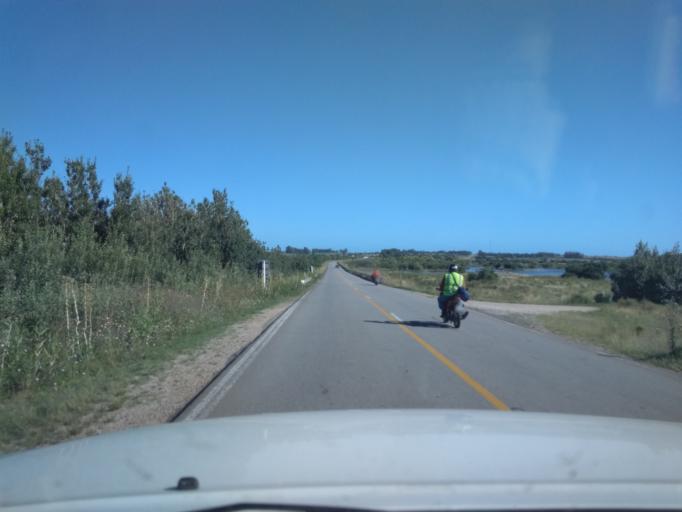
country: UY
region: Canelones
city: San Ramon
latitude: -34.3318
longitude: -55.9601
